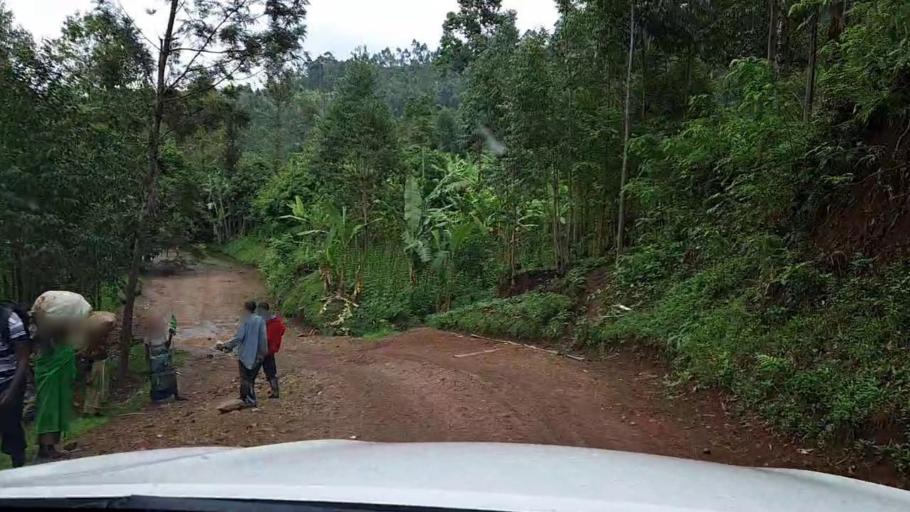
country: RW
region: Western Province
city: Cyangugu
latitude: -2.5510
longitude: 29.0379
